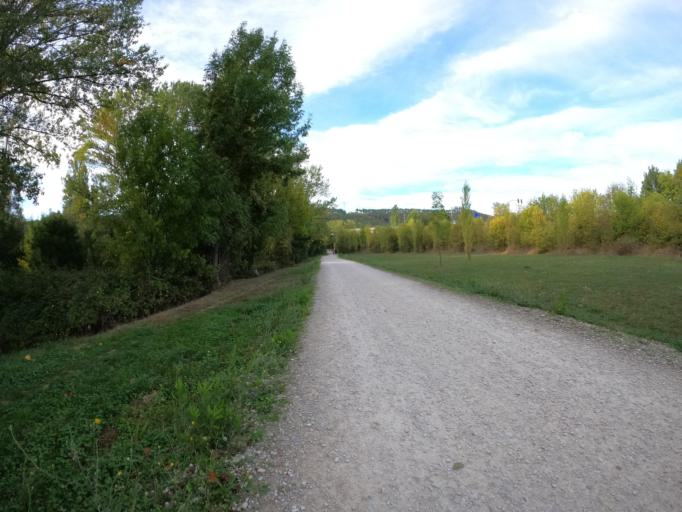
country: ES
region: Navarre
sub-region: Provincia de Navarra
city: Cizur Mayor
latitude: 42.8029
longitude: -1.7010
